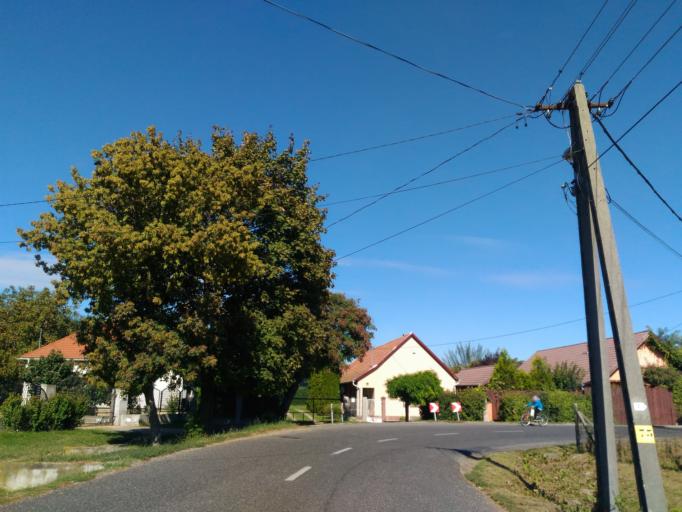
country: HU
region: Fejer
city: Ivancsa
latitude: 47.1429
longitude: 18.8340
